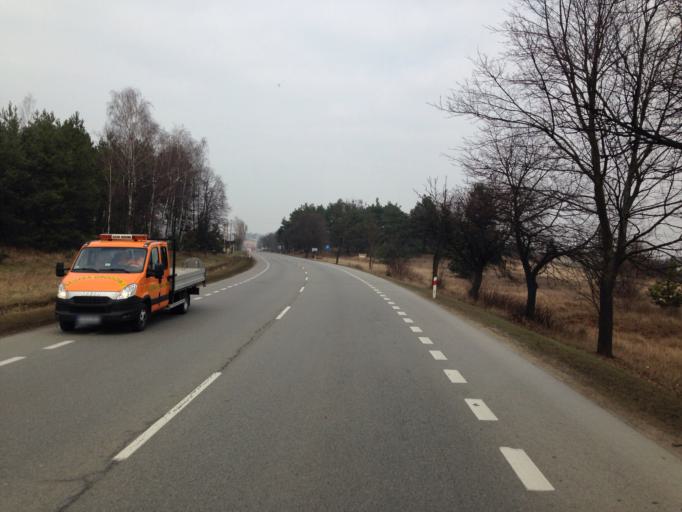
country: PL
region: Pomeranian Voivodeship
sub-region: Powiat tczewski
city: Gniew
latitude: 53.8201
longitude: 18.8129
